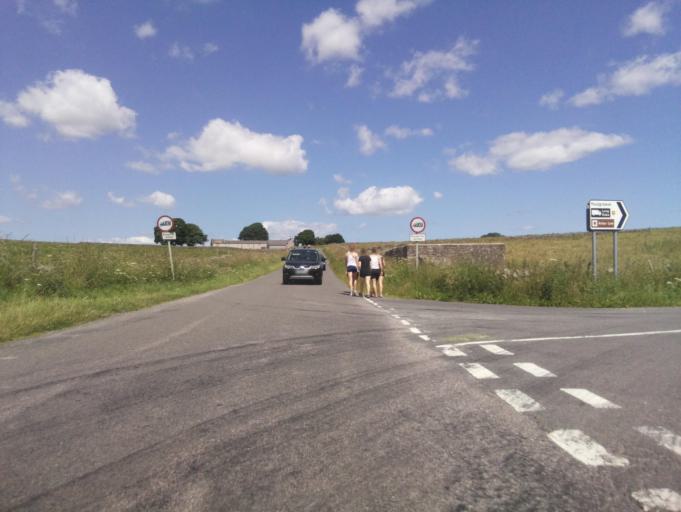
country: GB
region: England
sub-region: Derbyshire
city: Tideswell
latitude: 53.1718
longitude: -1.7794
